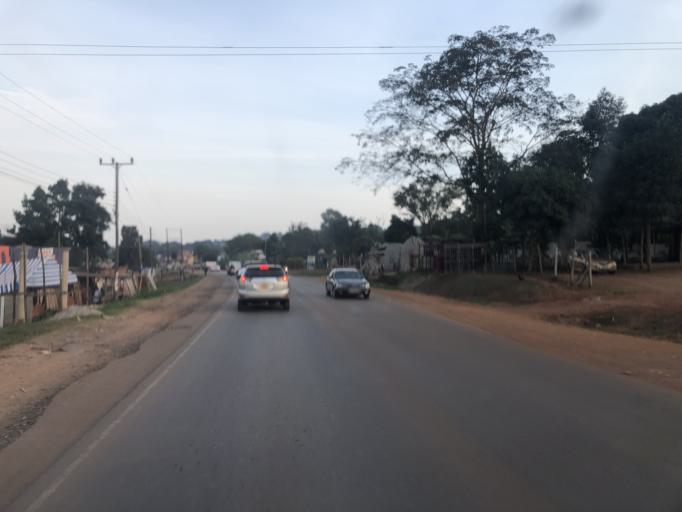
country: UG
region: Central Region
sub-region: Wakiso District
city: Kajansi
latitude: 0.2763
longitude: 32.4591
